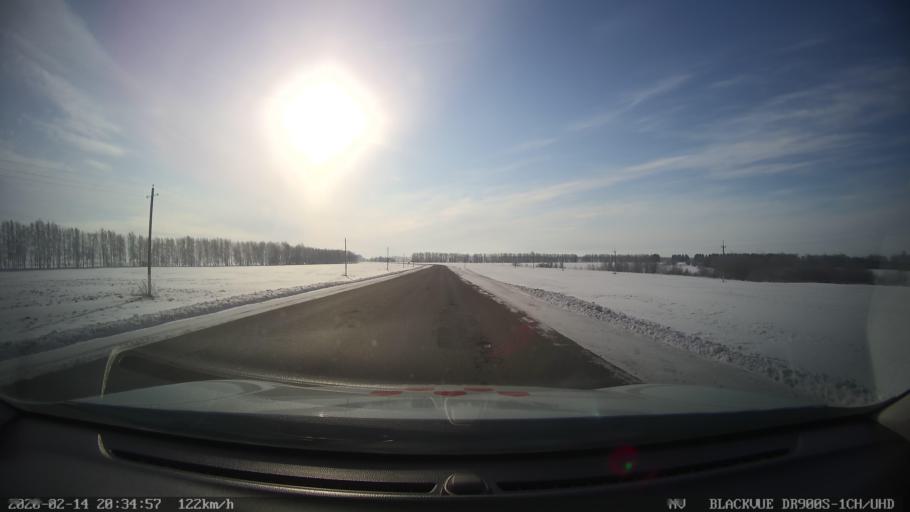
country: RU
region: Tatarstan
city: Kuybyshevskiy Zaton
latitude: 55.3903
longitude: 48.9794
